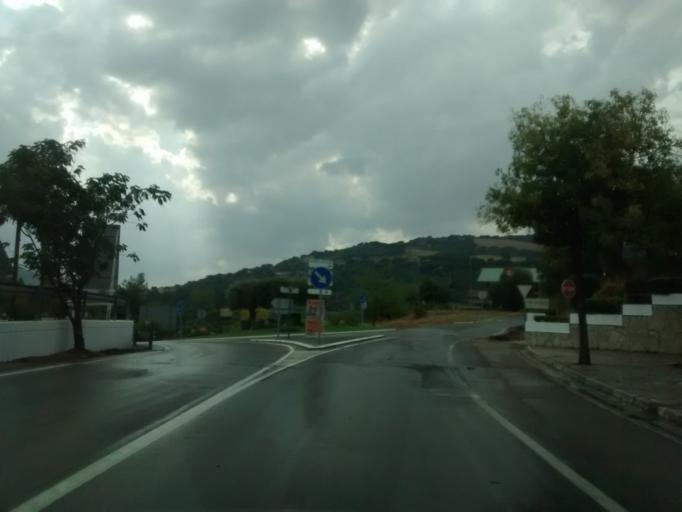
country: ES
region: Andalusia
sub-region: Provincia de Cadiz
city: El Bosque
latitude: 36.7580
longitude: -5.5113
